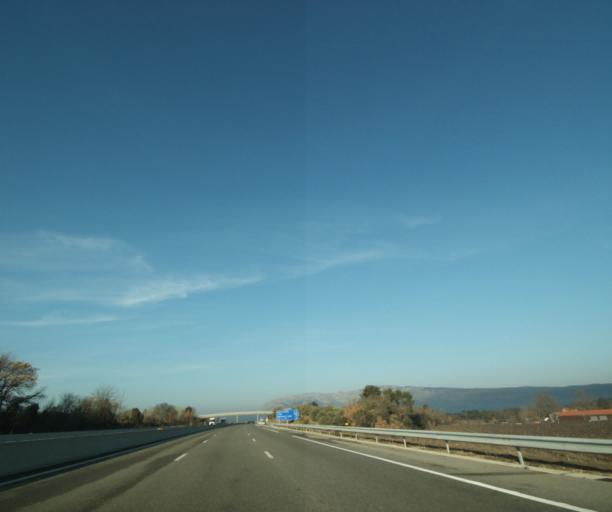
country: FR
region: Provence-Alpes-Cote d'Azur
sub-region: Departement du Var
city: Pourrieres
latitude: 43.4797
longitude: 5.7470
